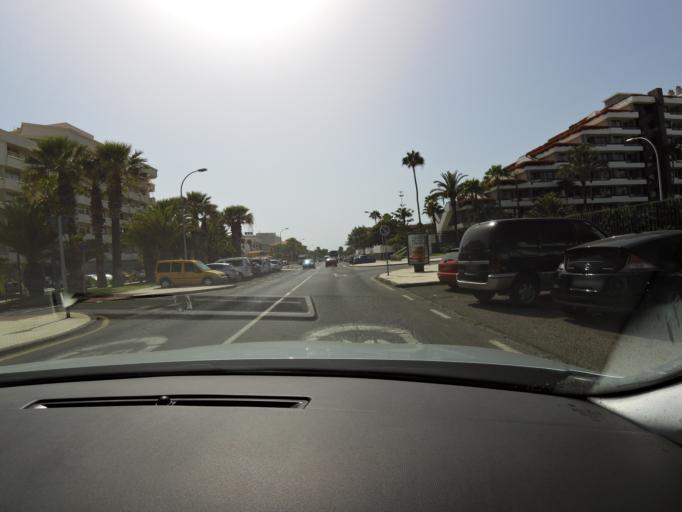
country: ES
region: Canary Islands
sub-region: Provincia de Santa Cruz de Tenerife
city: Playa de las Americas
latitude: 28.0574
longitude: -16.7307
